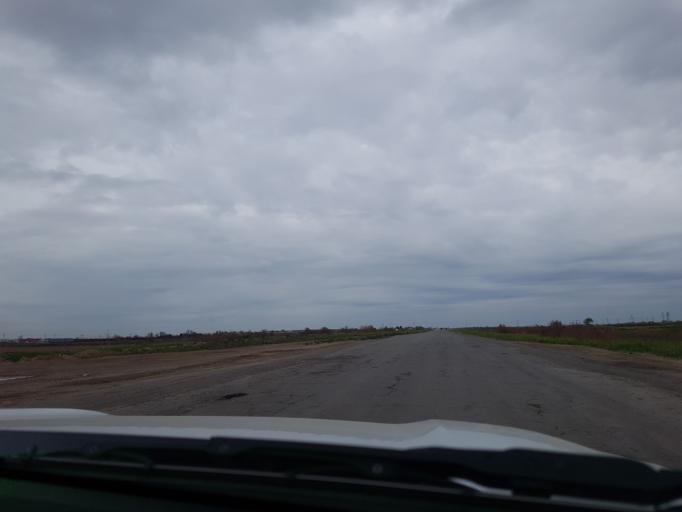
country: TM
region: Mary
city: Bayramaly
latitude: 37.7828
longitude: 62.5355
